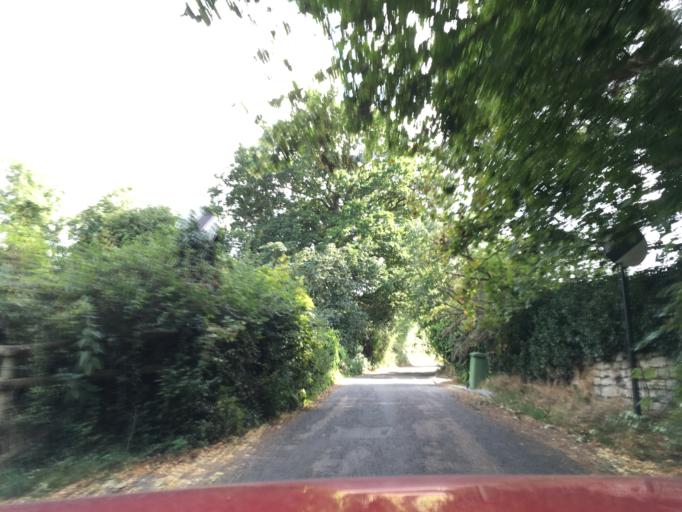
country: GB
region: England
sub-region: Kent
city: Maidstone
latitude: 51.2381
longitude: 0.5216
